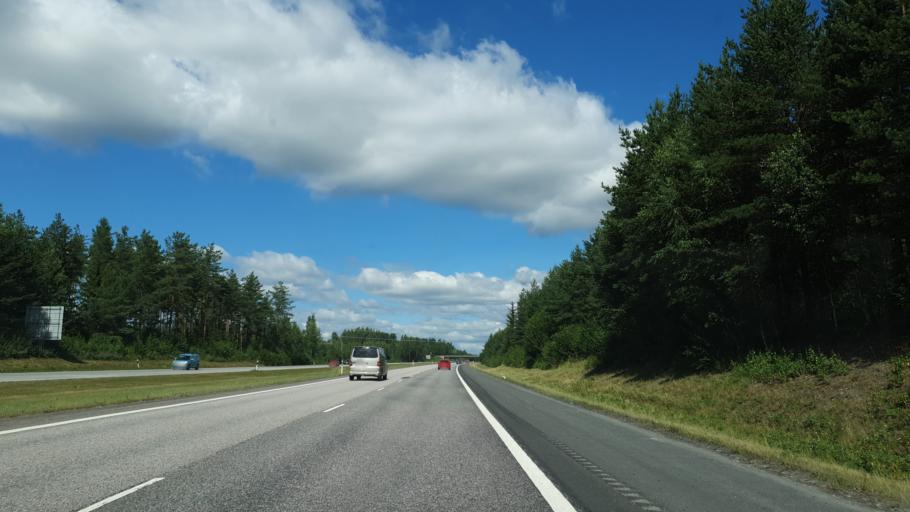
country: FI
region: Haeme
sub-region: Riihimaeki
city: Riihimaeki
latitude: 60.6970
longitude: 24.7427
